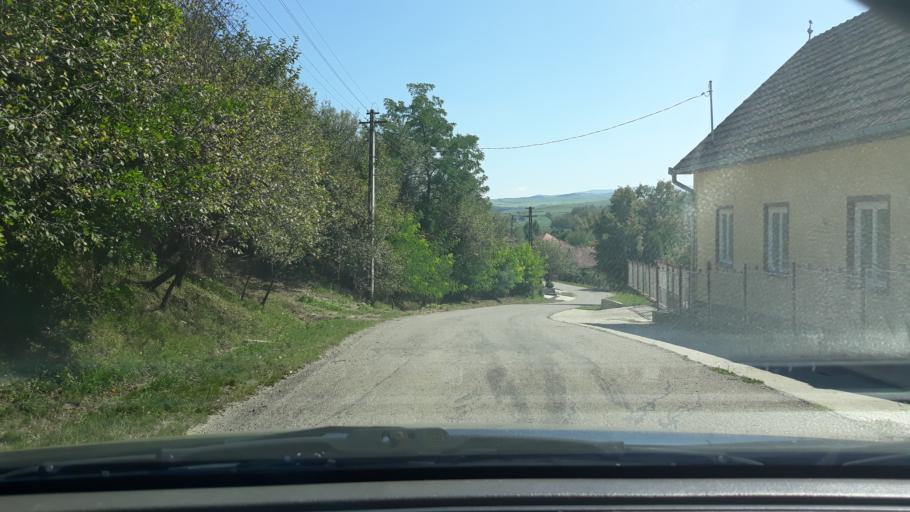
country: RO
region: Salaj
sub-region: Comuna Dobrin
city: Dobrin
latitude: 47.2961
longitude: 23.0922
